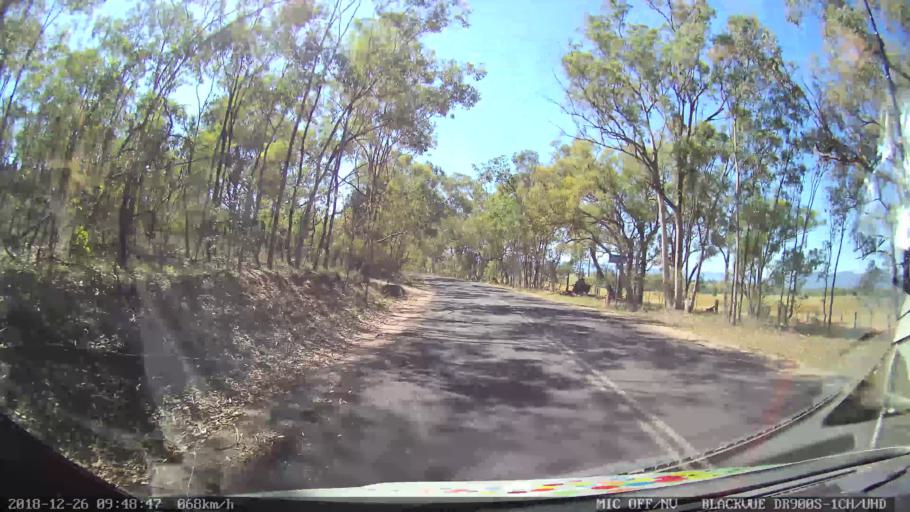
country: AU
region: New South Wales
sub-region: Mid-Western Regional
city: Kandos
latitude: -32.9897
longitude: 150.1172
